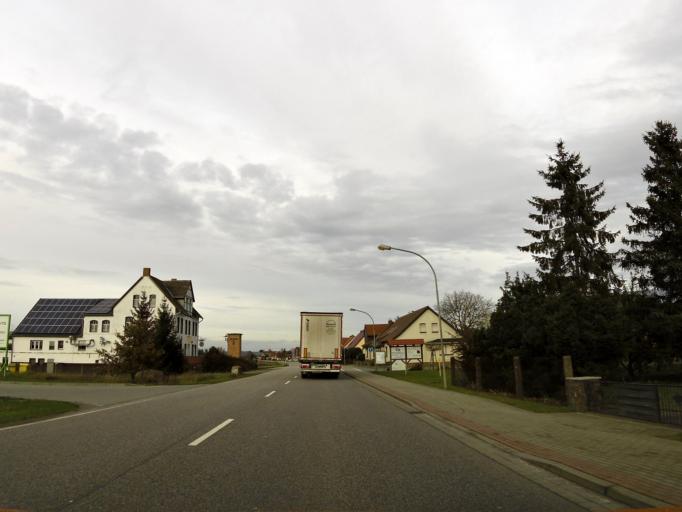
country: DE
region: Saxony-Anhalt
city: Pretzier
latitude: 52.7345
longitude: 11.2450
